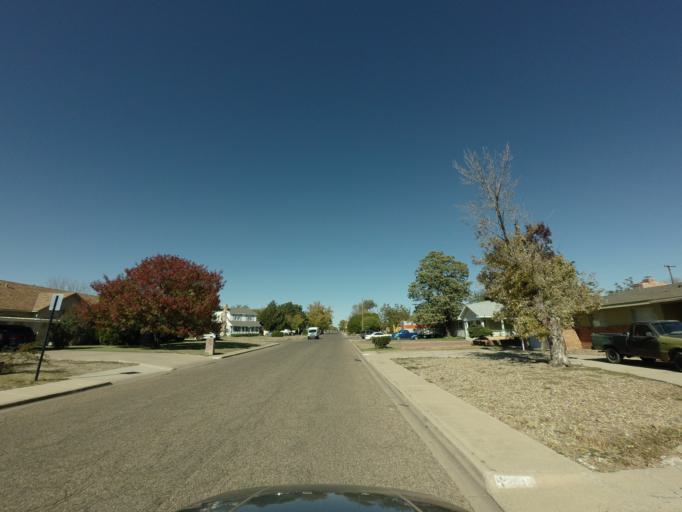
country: US
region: New Mexico
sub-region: Curry County
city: Clovis
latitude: 34.4218
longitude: -103.2003
